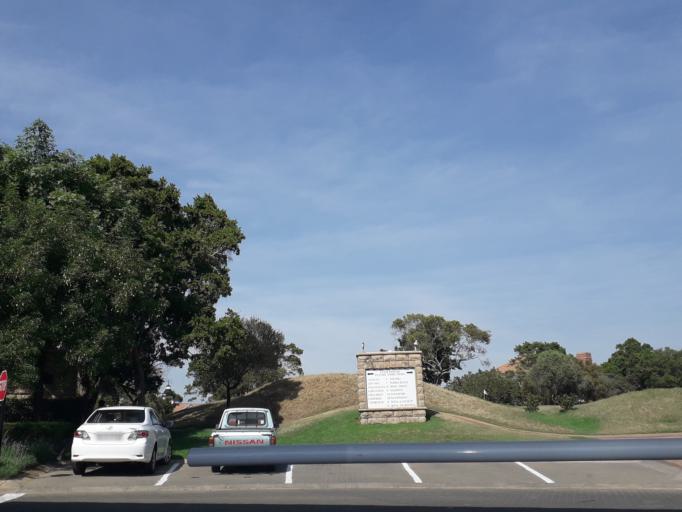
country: ZA
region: Gauteng
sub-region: City of Johannesburg Metropolitan Municipality
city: Diepsloot
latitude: -26.0154
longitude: 28.0037
